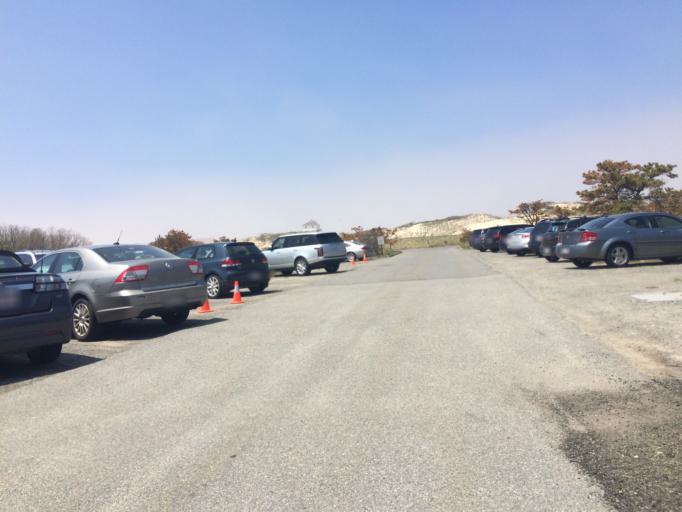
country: US
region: Massachusetts
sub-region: Barnstable County
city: Provincetown
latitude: 42.0763
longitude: -70.2171
